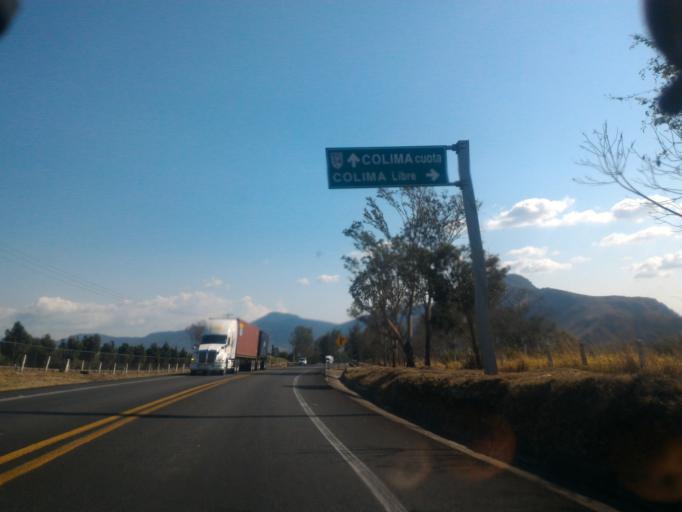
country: MX
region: Jalisco
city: Tuxpan
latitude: 19.5371
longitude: -103.4229
